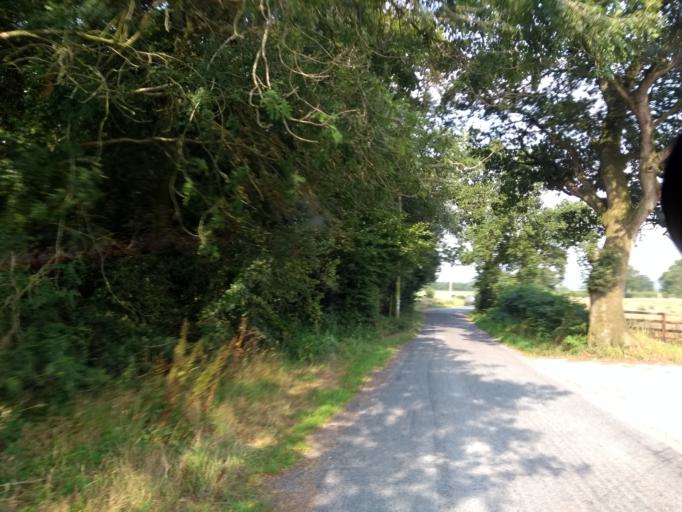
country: GB
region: England
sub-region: Somerset
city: Chard
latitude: 50.8806
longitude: -3.0306
